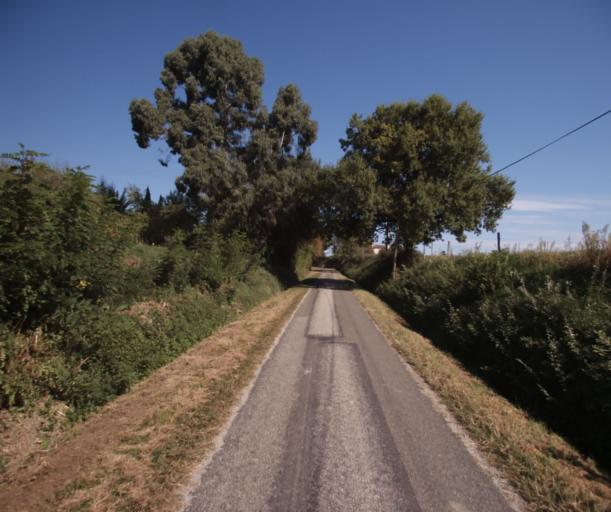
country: FR
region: Aquitaine
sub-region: Departement des Landes
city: Gabarret
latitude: 43.9424
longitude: -0.0129
